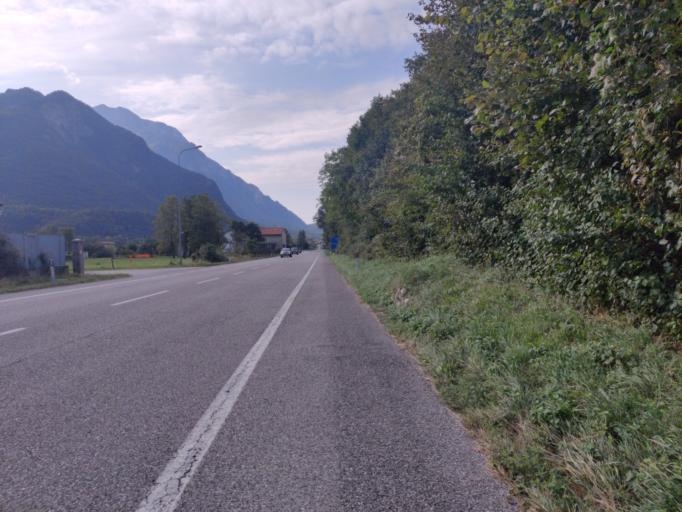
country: IT
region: Friuli Venezia Giulia
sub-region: Provincia di Udine
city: Venzone
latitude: 46.3418
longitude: 13.1397
